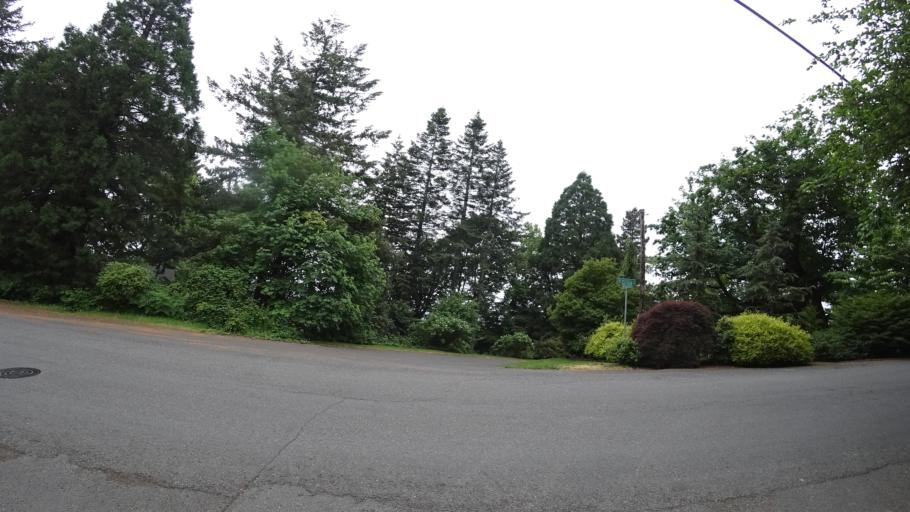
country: US
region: Oregon
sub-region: Multnomah County
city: Portland
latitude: 45.4858
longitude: -122.6927
